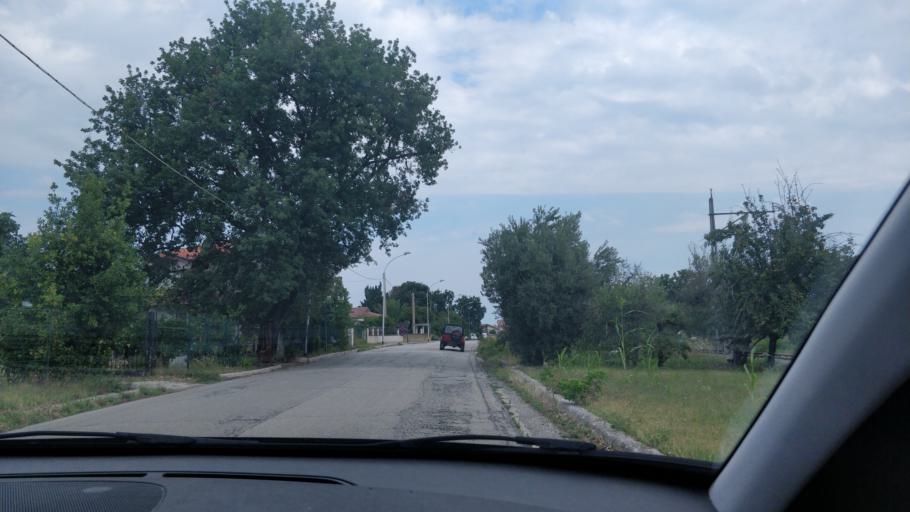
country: IT
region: Abruzzo
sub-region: Provincia di Chieti
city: San Vito Chietino
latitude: 42.2883
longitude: 14.4417
